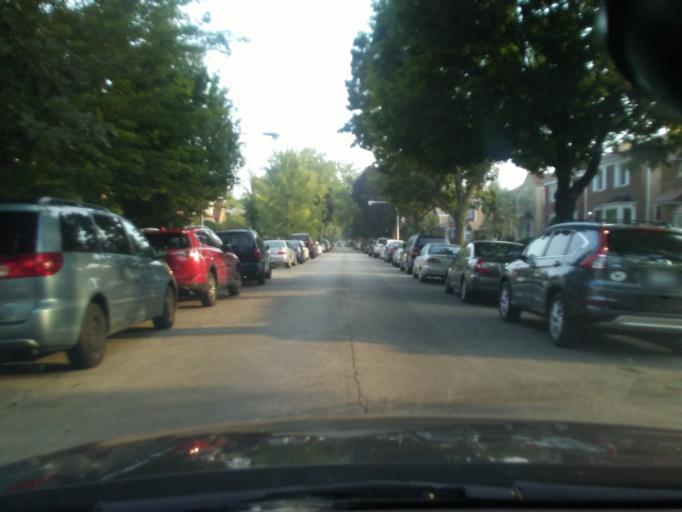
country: US
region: Illinois
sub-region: Cook County
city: Lincolnwood
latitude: 42.0013
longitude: -87.7046
